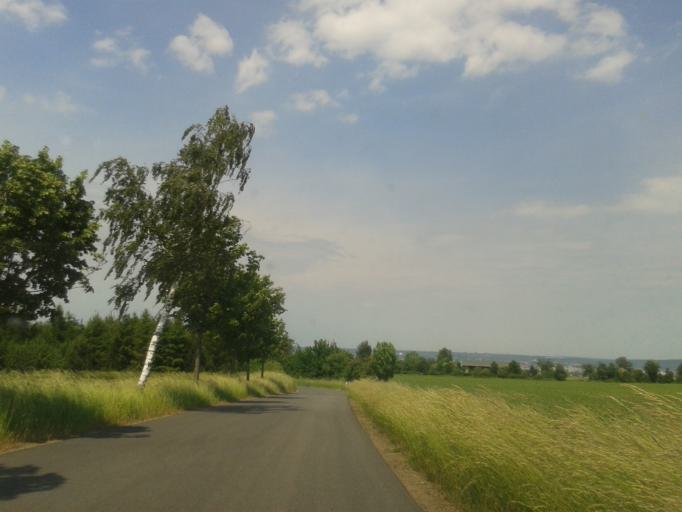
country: DE
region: Saxony
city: Bannewitz
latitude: 50.9916
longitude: 13.7295
